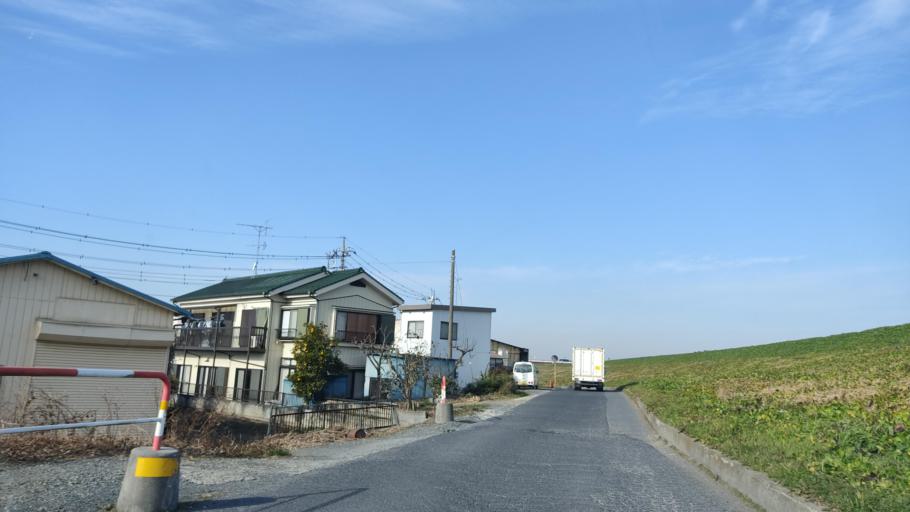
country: JP
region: Chiba
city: Nagareyama
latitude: 35.8667
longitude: 139.8950
